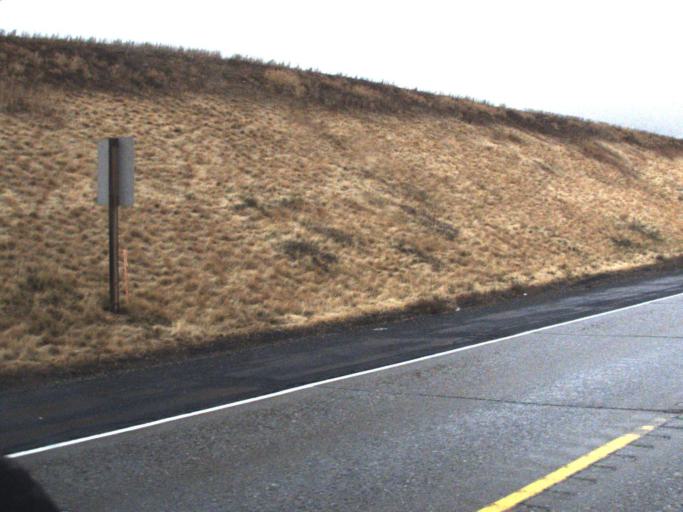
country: US
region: Washington
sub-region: Whitman County
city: Colfax
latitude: 47.1618
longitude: -117.3784
